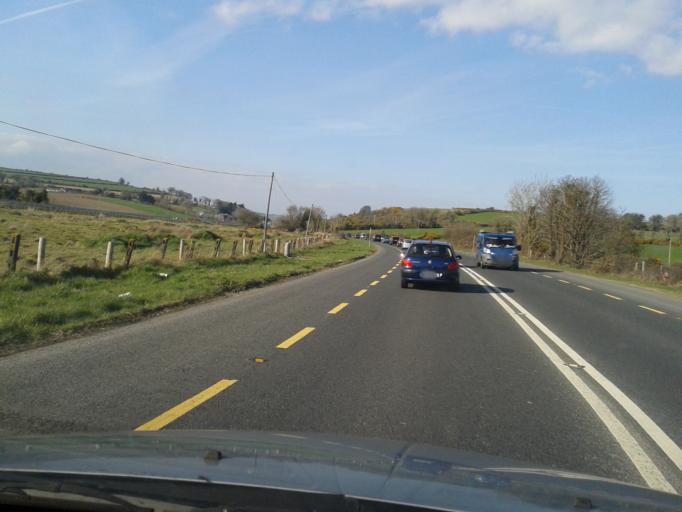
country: IE
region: Leinster
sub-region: Wicklow
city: Wicklow
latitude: 52.8865
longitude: -6.0980
